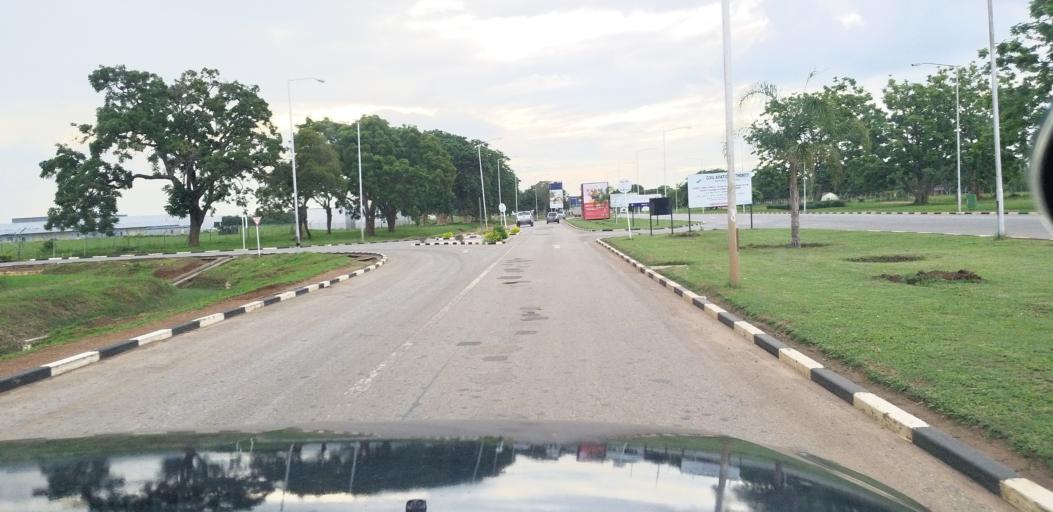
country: ZM
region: Lusaka
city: Lusaka
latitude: -15.3205
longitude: 28.4444
